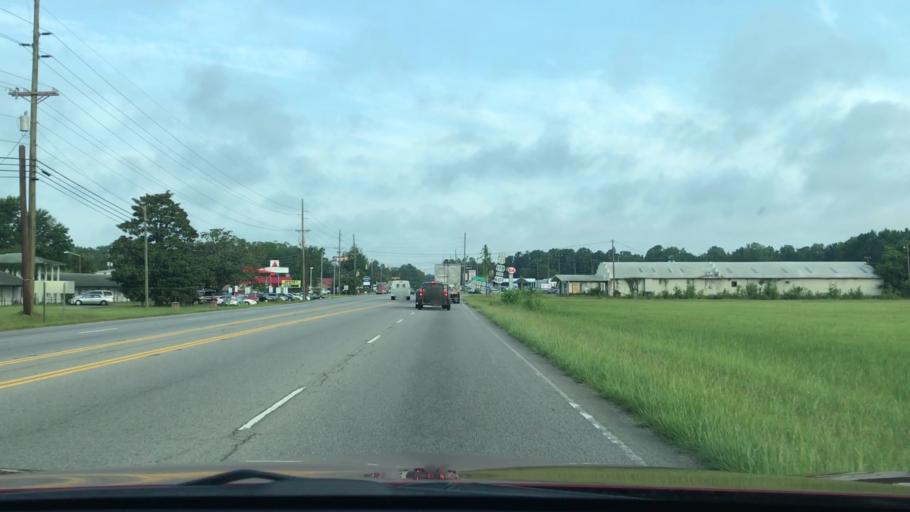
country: US
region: South Carolina
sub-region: Orangeburg County
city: Wilkinson Heights
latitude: 33.4846
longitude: -80.8296
